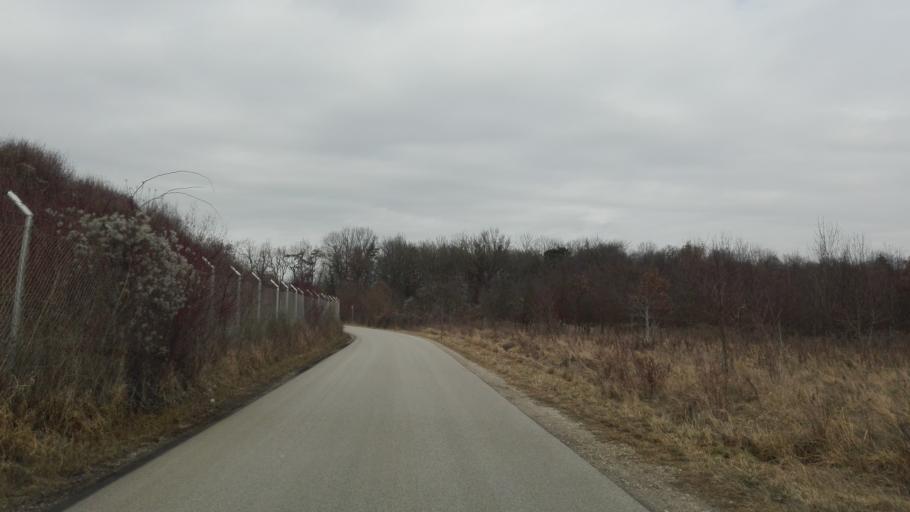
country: AT
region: Upper Austria
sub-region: Politischer Bezirk Linz-Land
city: Traun
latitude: 48.2333
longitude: 14.2177
